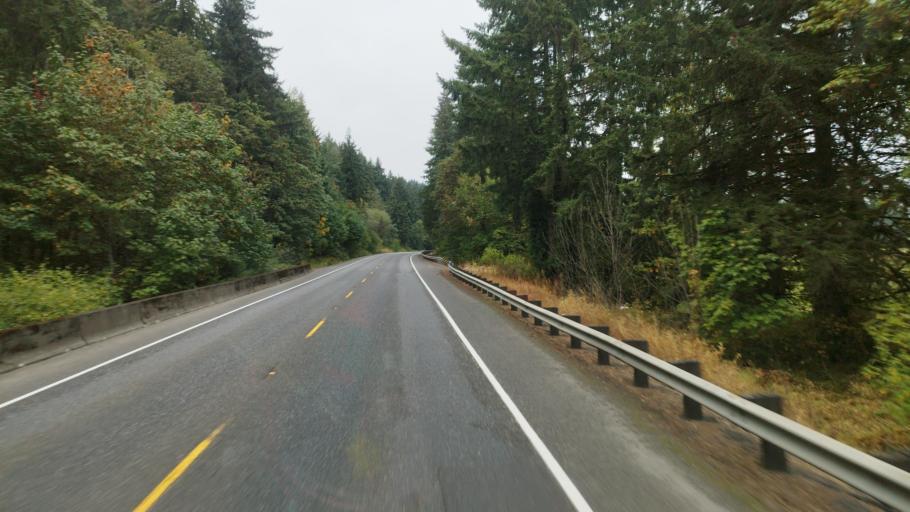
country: US
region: Washington
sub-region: Cowlitz County
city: Kalama
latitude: 45.9797
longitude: -122.8683
